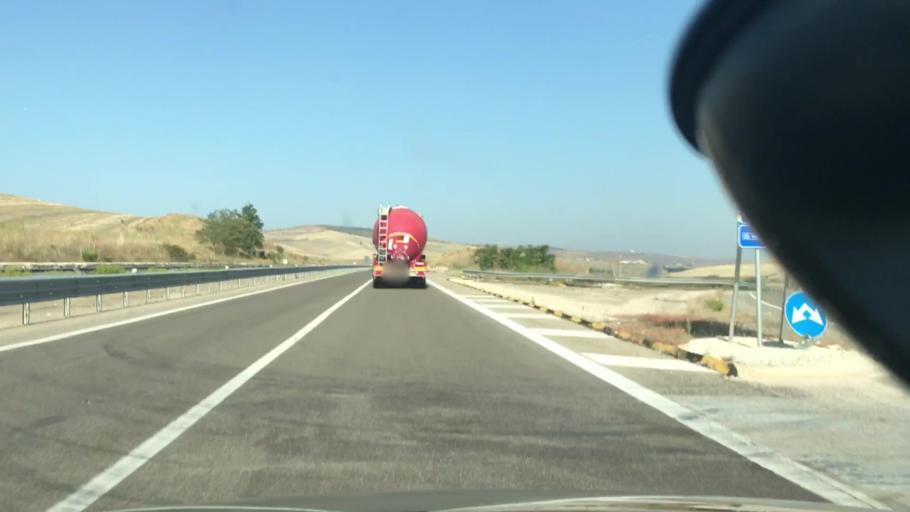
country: IT
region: Basilicate
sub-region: Provincia di Matera
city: Irsina
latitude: 40.7865
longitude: 16.2945
